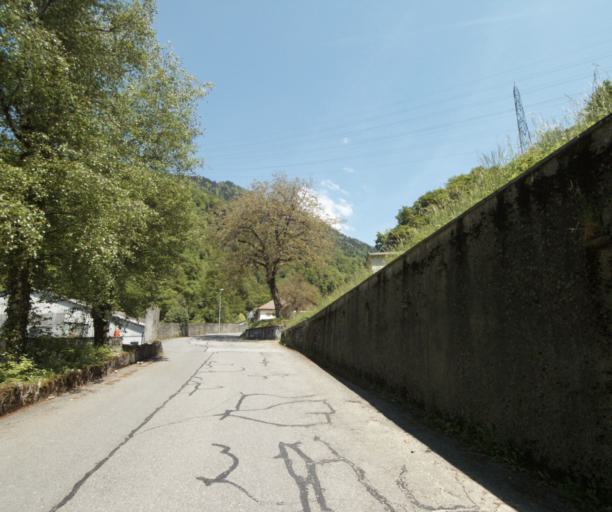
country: CH
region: Vaud
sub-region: Aigle District
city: Villeneuve
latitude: 46.4024
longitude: 6.9383
